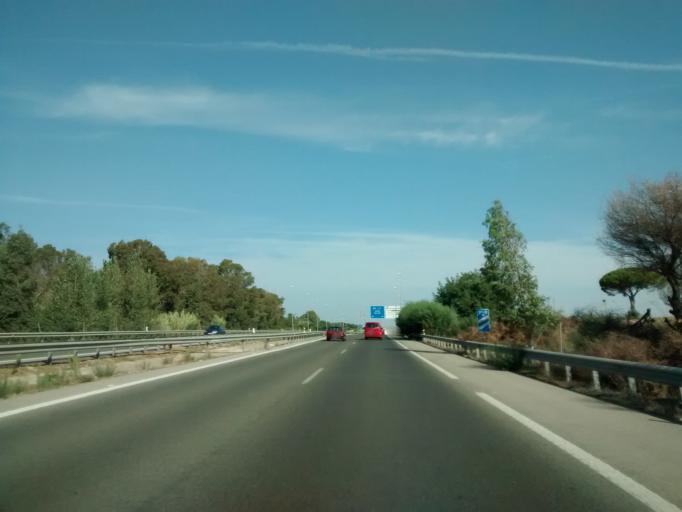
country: ES
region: Andalusia
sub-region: Provincia de Cadiz
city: Chiclana de la Frontera
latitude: 36.3936
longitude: -6.1220
